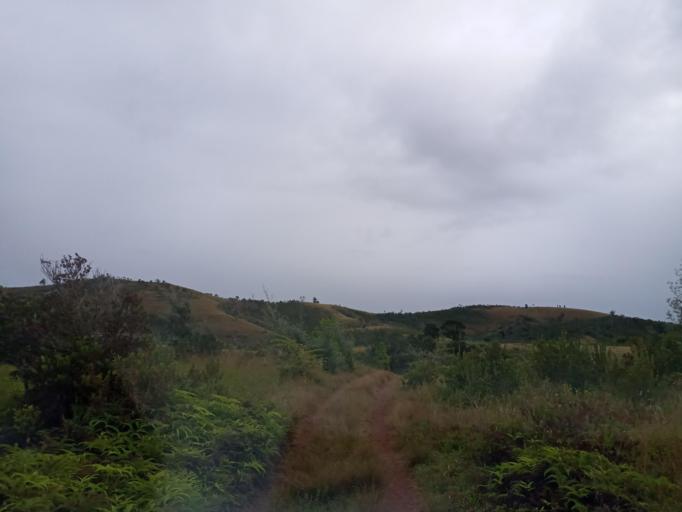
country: MG
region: Atsimo-Atsinanana
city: Vohipaho
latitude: -23.9926
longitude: 47.4023
